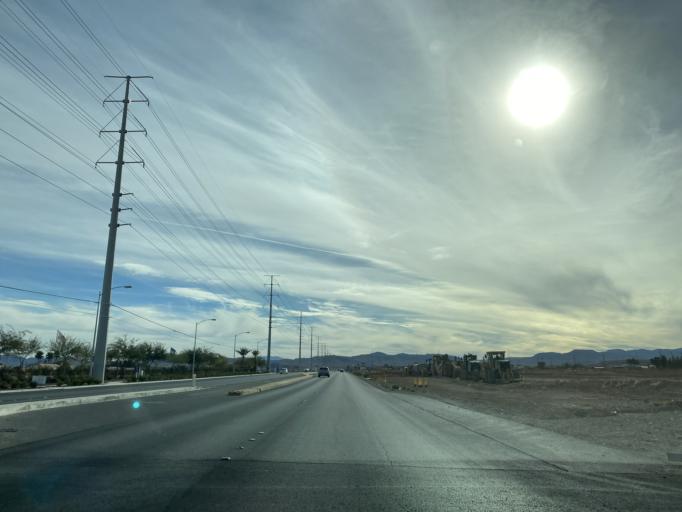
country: US
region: Nevada
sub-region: Clark County
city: Enterprise
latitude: 36.0304
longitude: -115.2435
